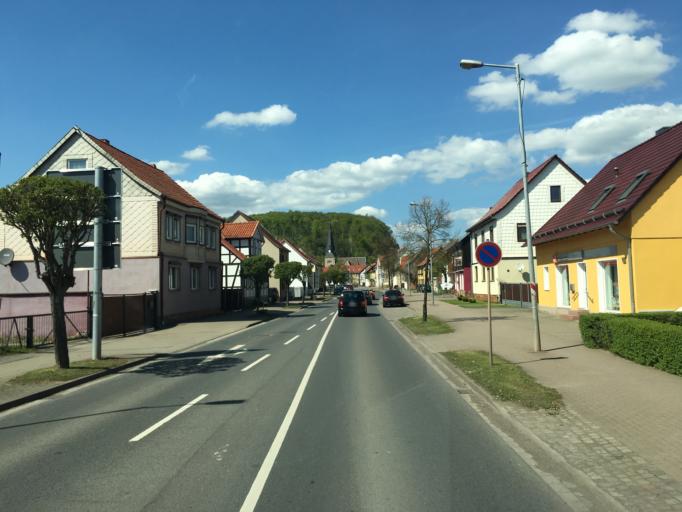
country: DE
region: Thuringia
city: Niedersachswerfen
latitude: 51.5510
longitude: 10.7674
